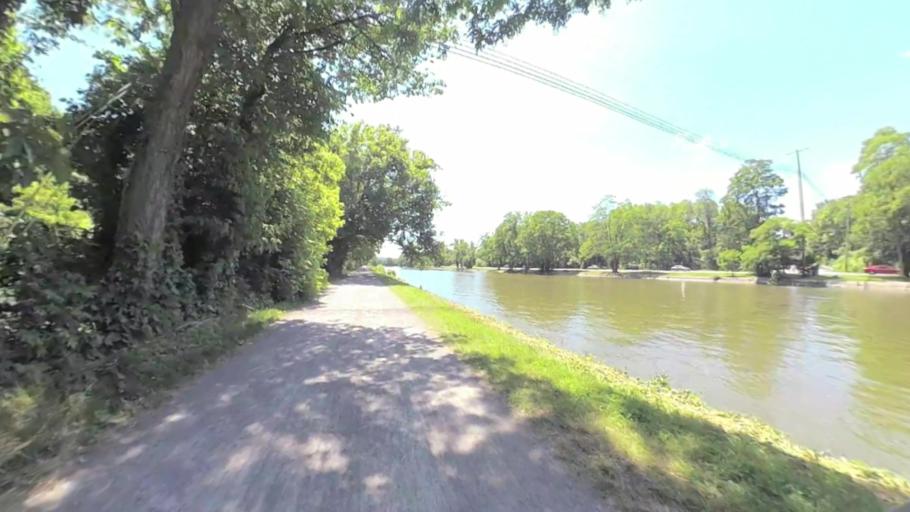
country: US
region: New York
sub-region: Monroe County
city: Pittsford
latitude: 43.0773
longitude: -77.4978
